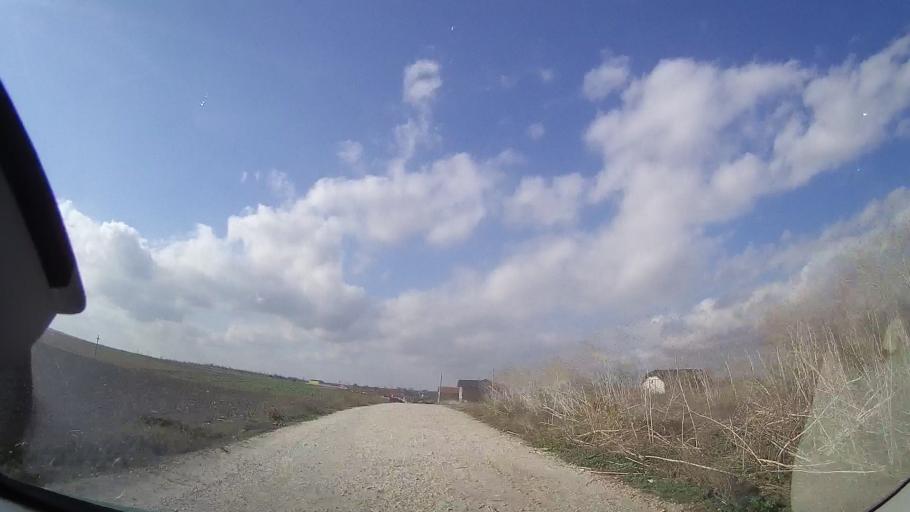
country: RO
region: Constanta
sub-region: Comuna Douazeci si Trei August
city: Douazeci si Trei August
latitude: 43.9120
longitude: 28.5907
